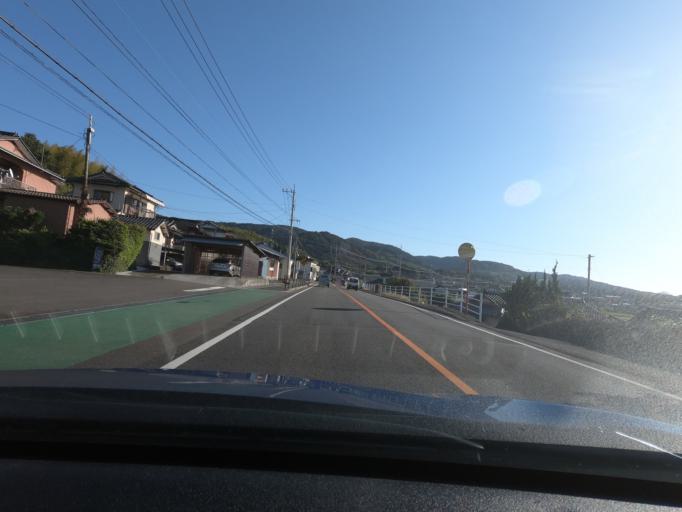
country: JP
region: Kumamoto
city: Minamata
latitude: 32.1780
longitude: 130.3835
